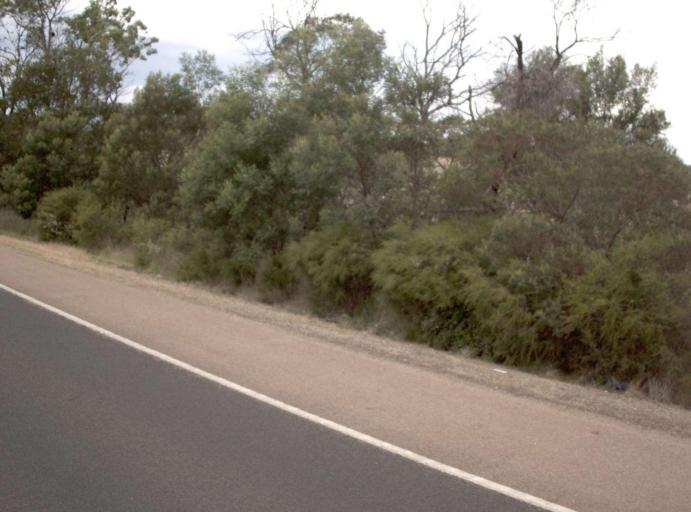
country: AU
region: Victoria
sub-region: East Gippsland
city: Bairnsdale
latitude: -37.9011
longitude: 147.6745
